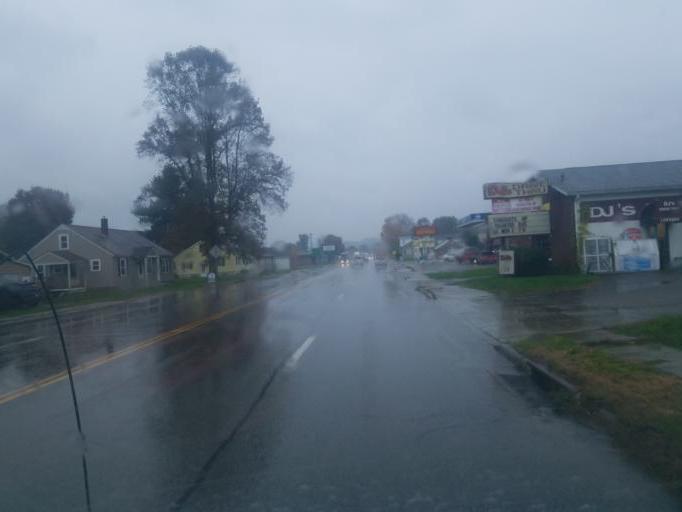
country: US
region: Ohio
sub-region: Muskingum County
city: Pleasant Grove
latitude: 39.8735
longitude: -81.9183
